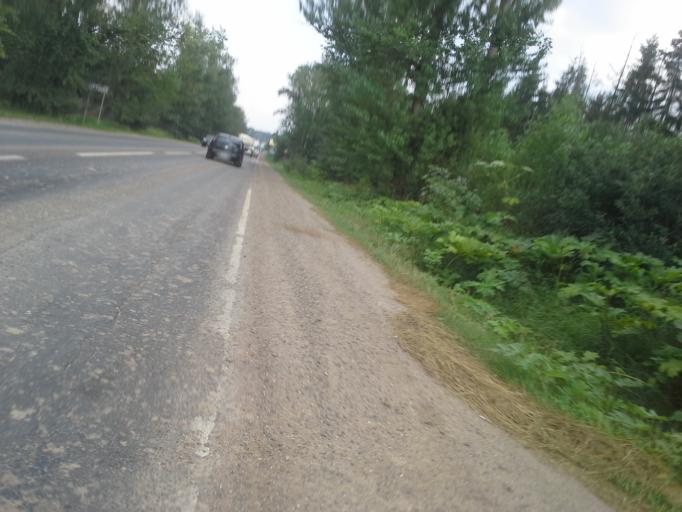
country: RU
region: Moskovskaya
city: Istra
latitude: 55.9301
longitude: 36.9416
